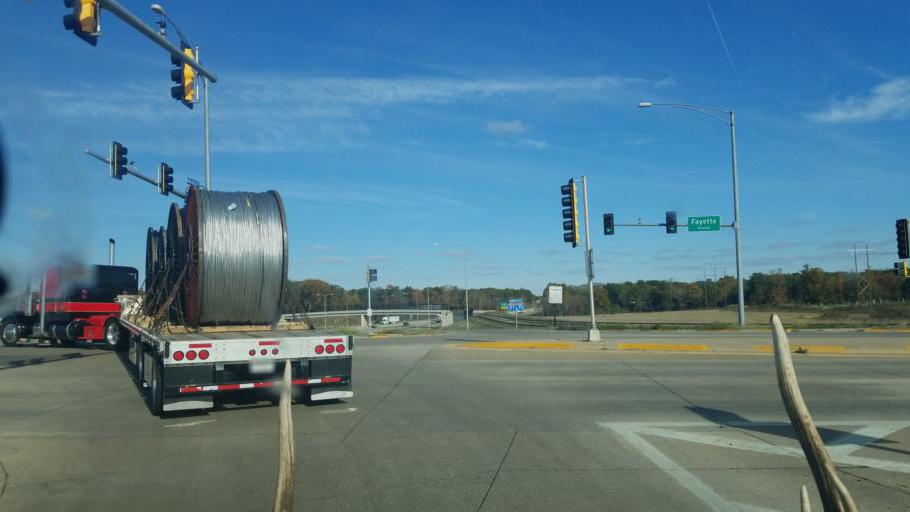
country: US
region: Illinois
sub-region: Effingham County
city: Effingham
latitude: 39.1204
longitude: -88.5672
